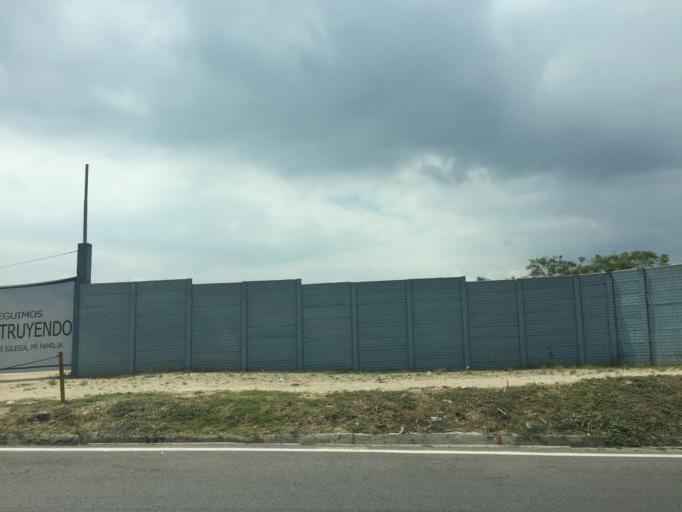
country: GT
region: Guatemala
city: Petapa
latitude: 14.5241
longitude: -90.5532
